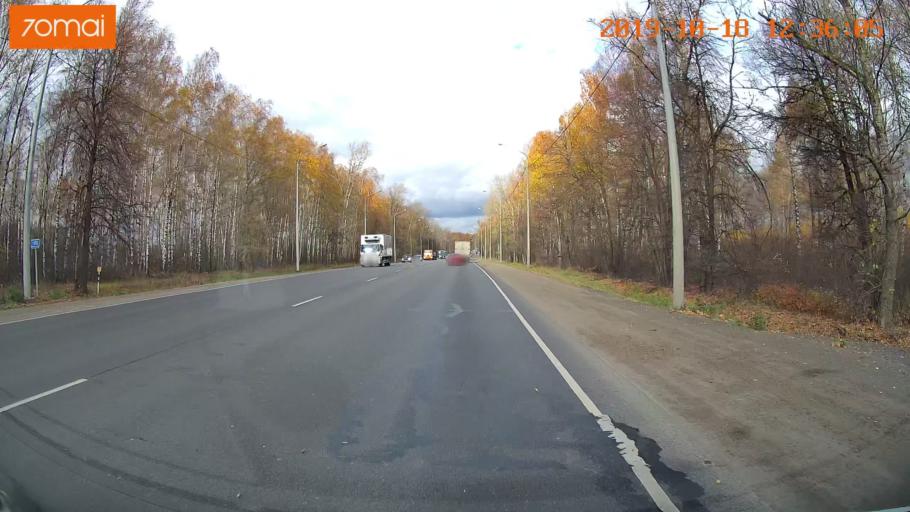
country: RU
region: Rjazan
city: Ryazan'
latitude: 54.6314
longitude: 39.6345
